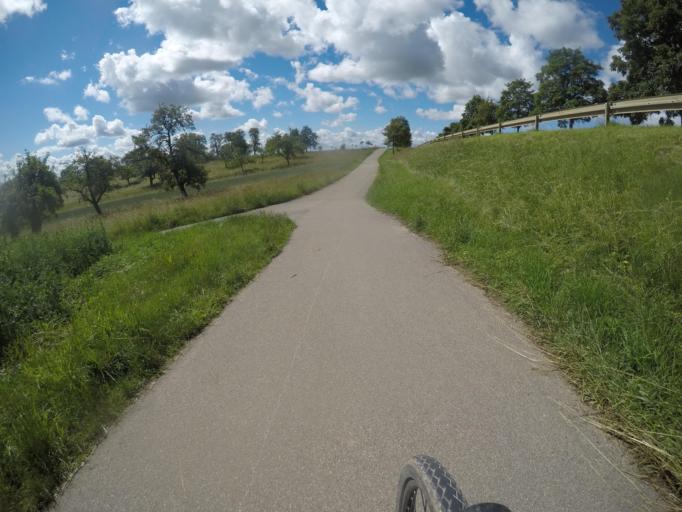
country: DE
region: Baden-Wuerttemberg
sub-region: Regierungsbezirk Stuttgart
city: Unterjettingen
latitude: 48.5595
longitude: 8.7833
